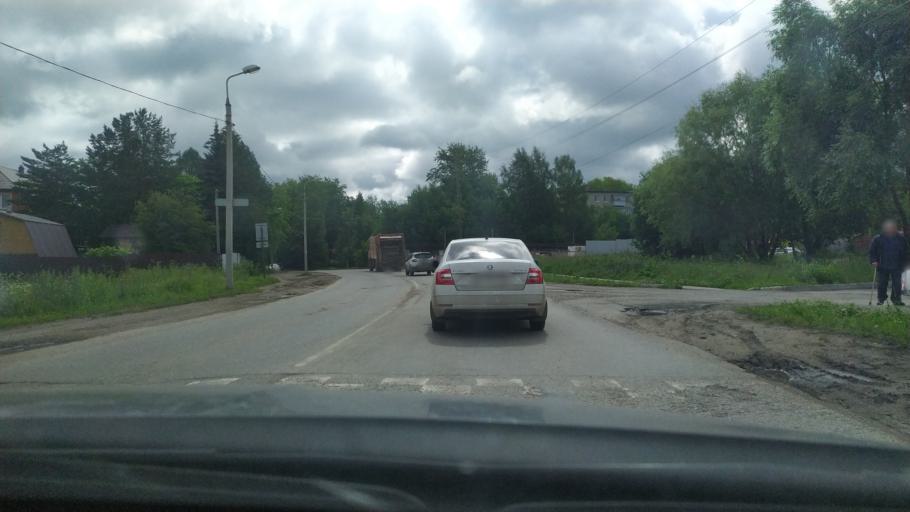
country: RU
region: Perm
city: Froly
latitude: 57.9764
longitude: 56.3156
